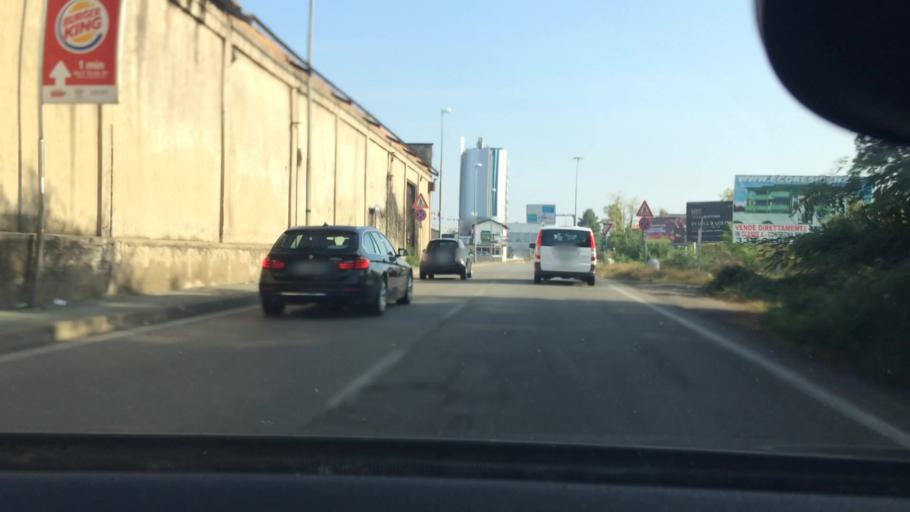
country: IT
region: Lombardy
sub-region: Citta metropolitana di Milano
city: Cerro Maggiore
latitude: 45.5985
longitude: 8.9433
